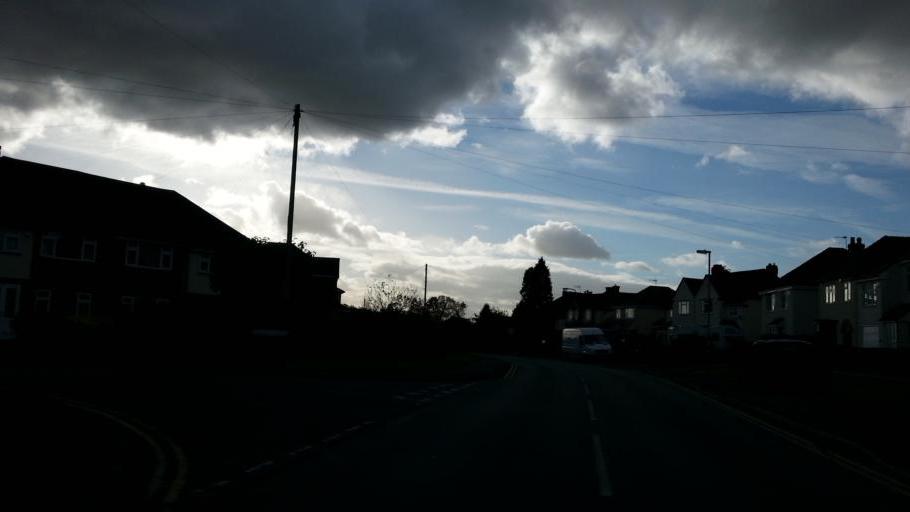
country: GB
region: England
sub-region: Staffordshire
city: Cannock
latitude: 52.6861
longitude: -2.0406
